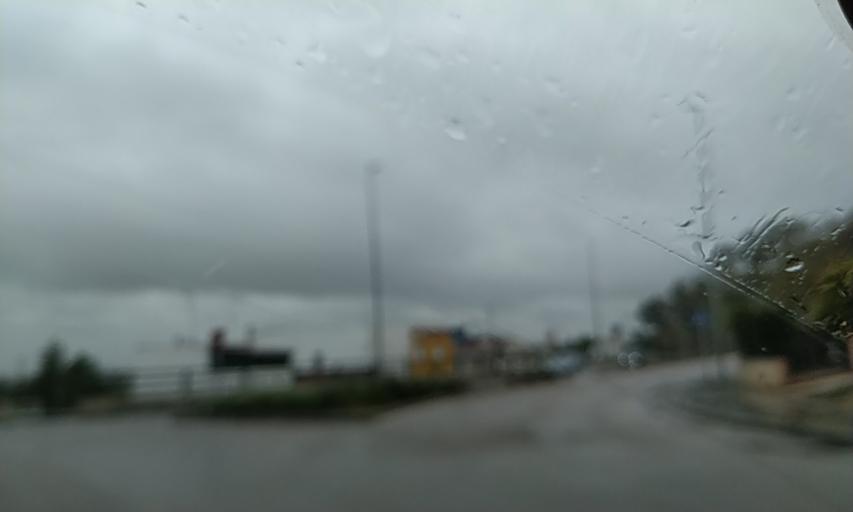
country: ES
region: Extremadura
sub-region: Provincia de Badajoz
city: Badajoz
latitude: 38.8913
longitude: -6.9716
